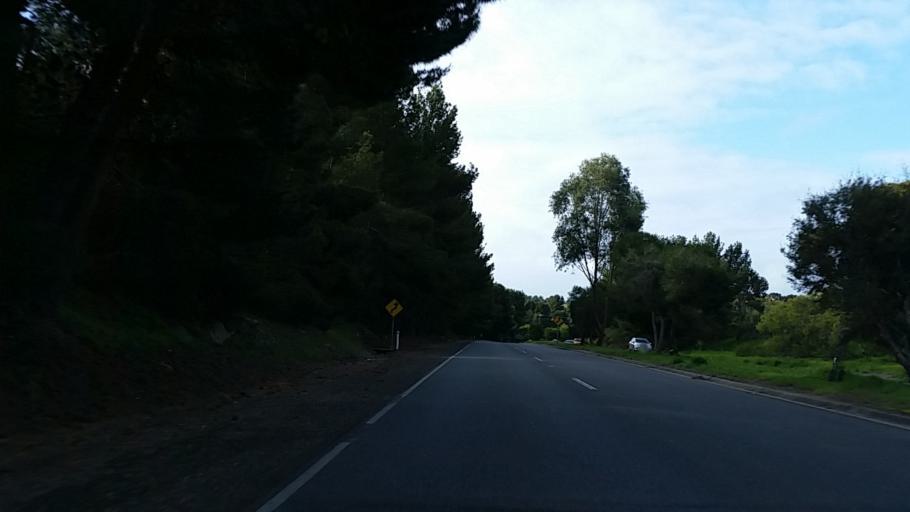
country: AU
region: South Australia
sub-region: Onkaparinga
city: Reynella
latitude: -35.0917
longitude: 138.5371
